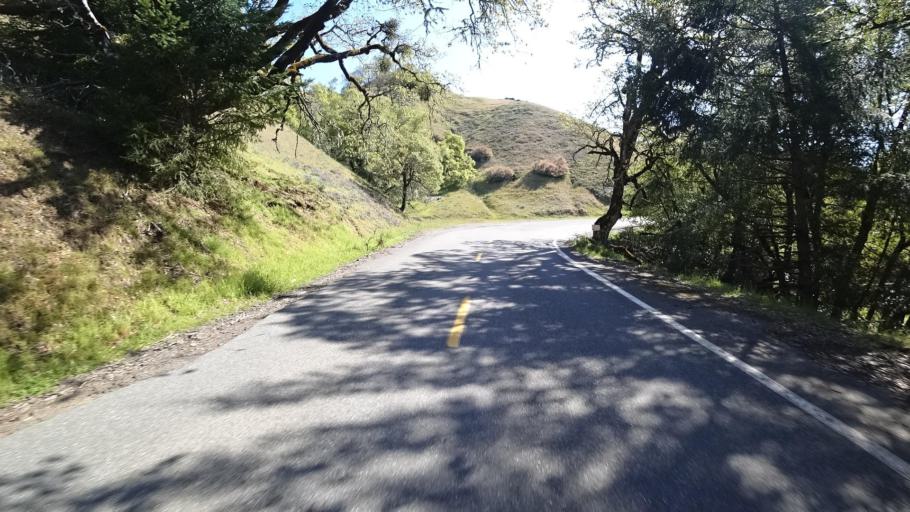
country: US
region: California
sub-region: Humboldt County
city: Redway
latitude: 40.1047
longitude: -123.6938
